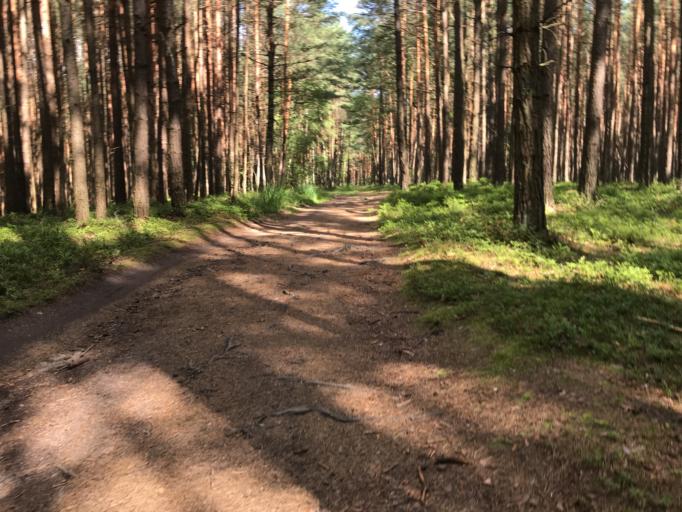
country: CZ
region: Jihocesky
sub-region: Okres Jindrichuv Hradec
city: Trebon
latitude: 48.9899
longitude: 14.7168
